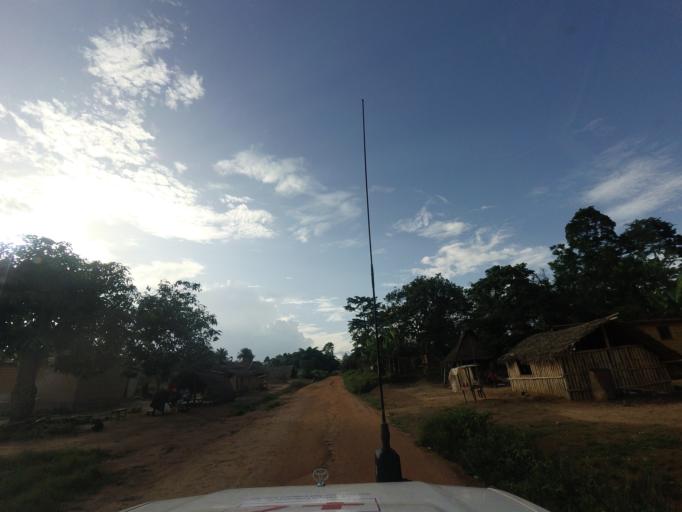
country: GN
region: Nzerekore
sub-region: Nzerekore Prefecture
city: Nzerekore
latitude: 7.6809
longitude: -8.8126
